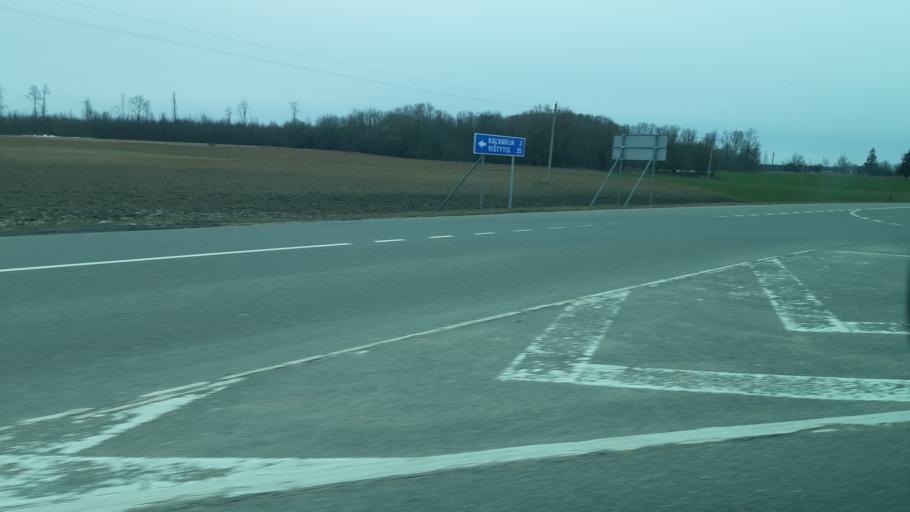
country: LT
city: Kalvarija
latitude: 54.4166
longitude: 23.2020
